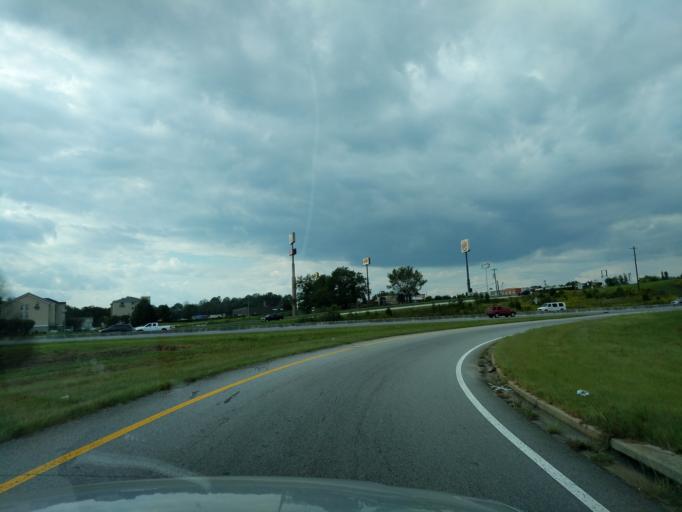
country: US
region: South Carolina
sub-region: Anderson County
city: Powdersville
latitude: 34.7736
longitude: -82.4637
